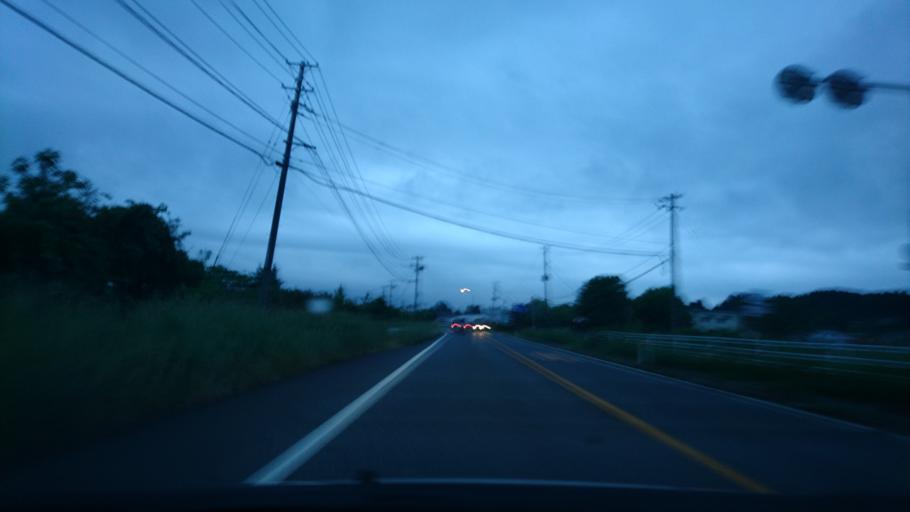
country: JP
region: Iwate
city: Ichinoseki
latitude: 38.8184
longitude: 141.0771
